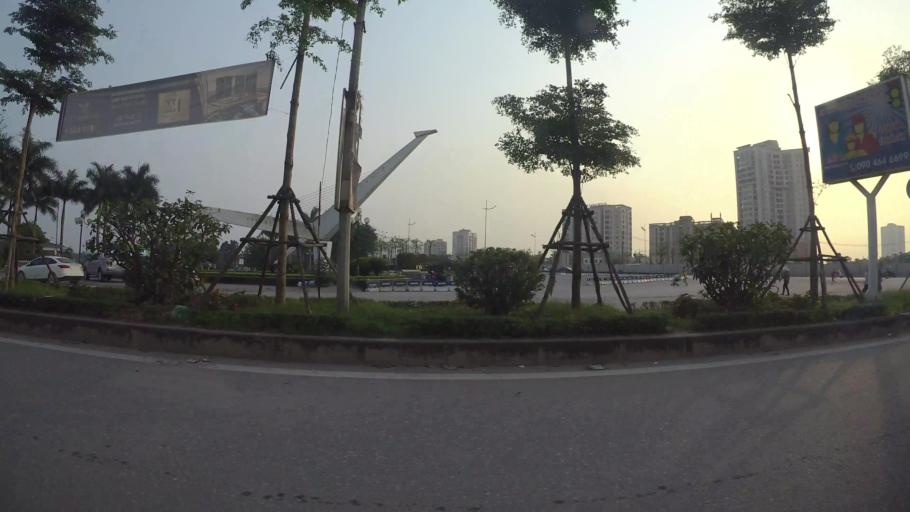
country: VN
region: Ha Noi
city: Tay Ho
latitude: 21.0683
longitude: 105.7861
